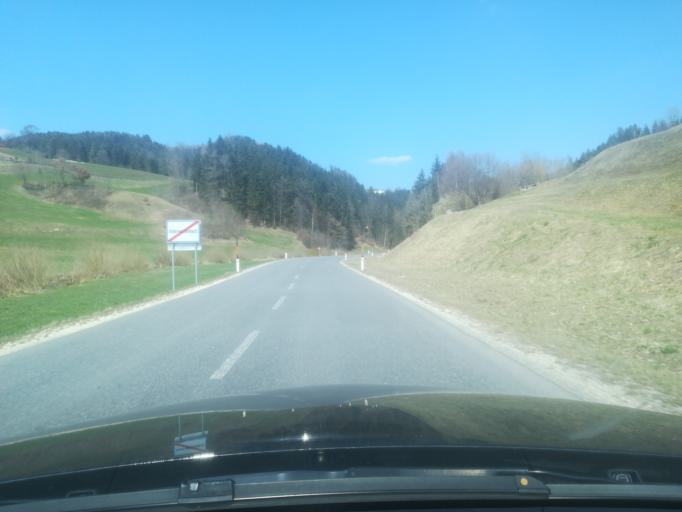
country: AT
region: Upper Austria
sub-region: Politischer Bezirk Perg
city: Sankt Georgen am Walde
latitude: 48.4399
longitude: 14.7823
